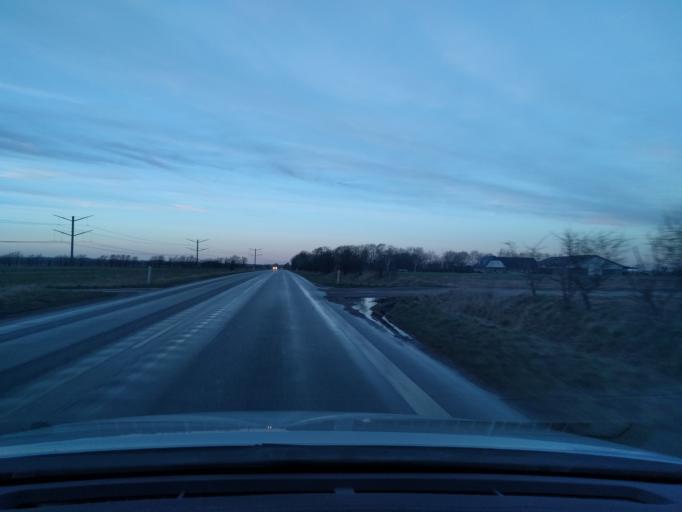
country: DK
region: South Denmark
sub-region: Tonder Kommune
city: Toftlund
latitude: 55.2564
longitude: 9.1463
